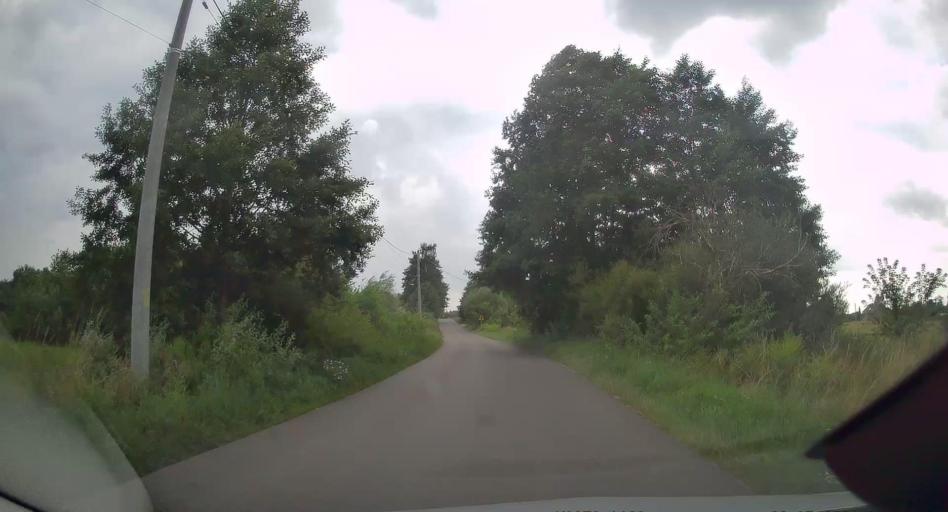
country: PL
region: Lodz Voivodeship
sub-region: Powiat rawski
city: Rawa Mazowiecka
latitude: 51.7502
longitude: 20.2154
